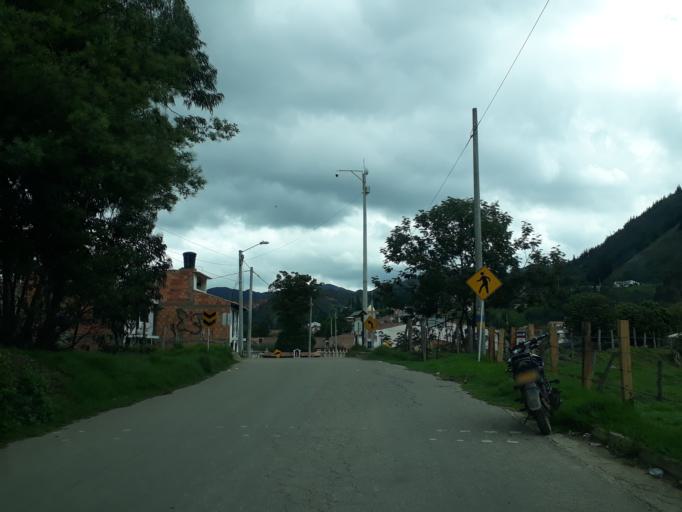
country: CO
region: Cundinamarca
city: Cucunuba
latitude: 5.2470
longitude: -73.7677
